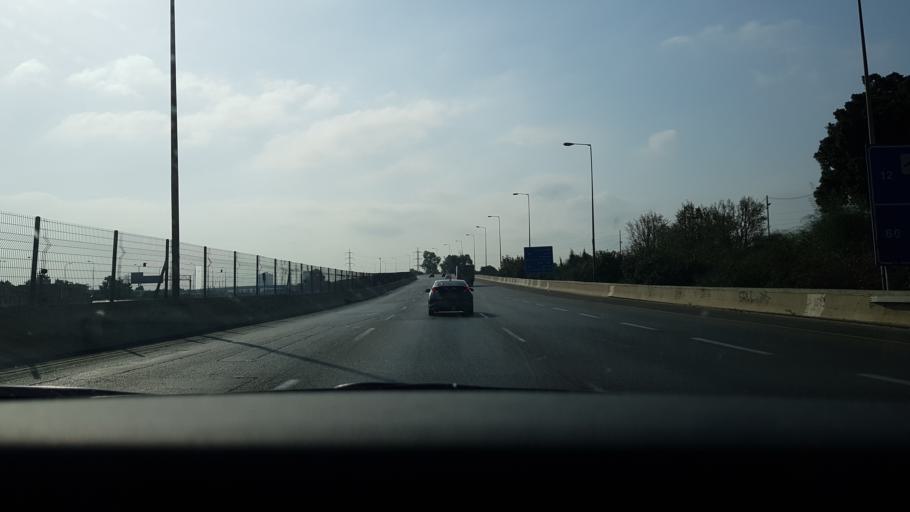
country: IL
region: Tel Aviv
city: Azor
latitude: 32.0449
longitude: 34.7874
